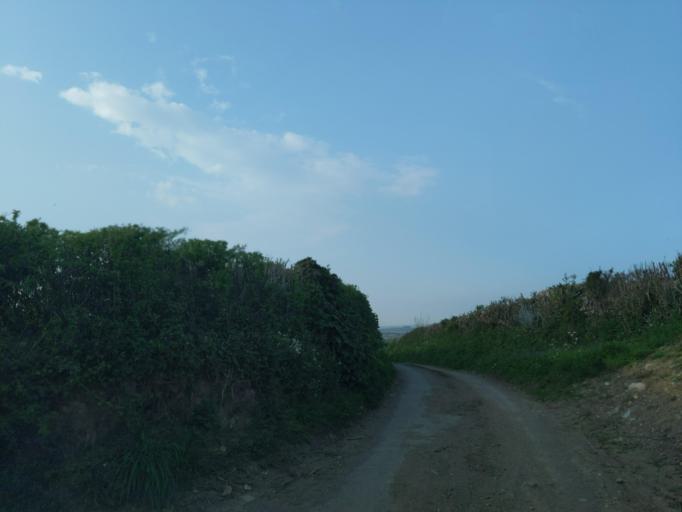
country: GB
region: England
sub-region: Devon
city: Plympton
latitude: 50.3572
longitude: -4.0384
